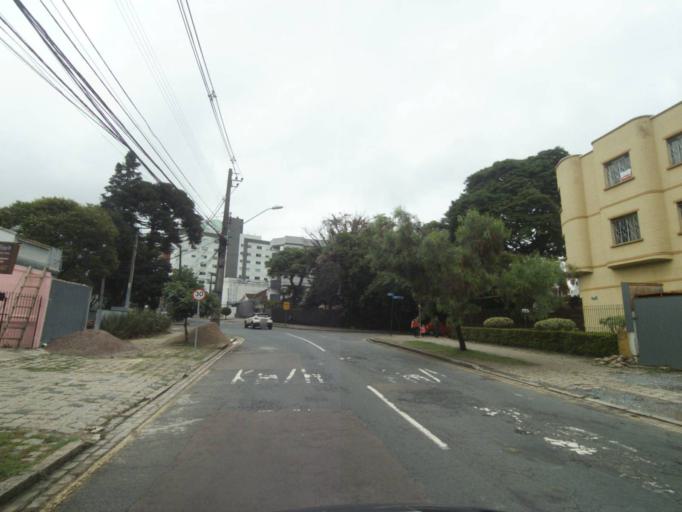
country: BR
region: Parana
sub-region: Curitiba
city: Curitiba
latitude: -25.4129
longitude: -49.2604
